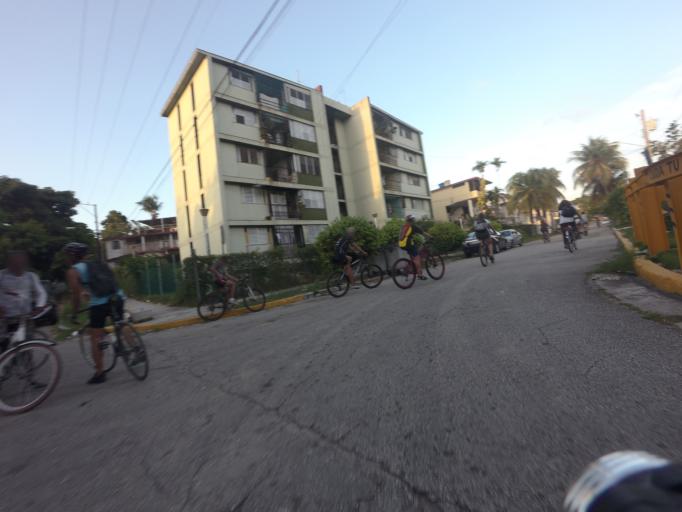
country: CU
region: La Habana
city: Havana
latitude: 23.1164
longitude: -82.4055
